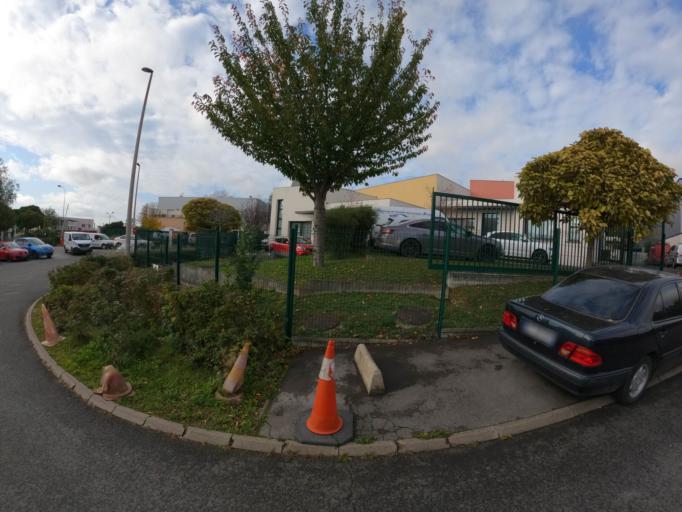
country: FR
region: Ile-de-France
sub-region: Departement de Seine-et-Marne
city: Chelles
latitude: 48.8910
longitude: 2.5902
